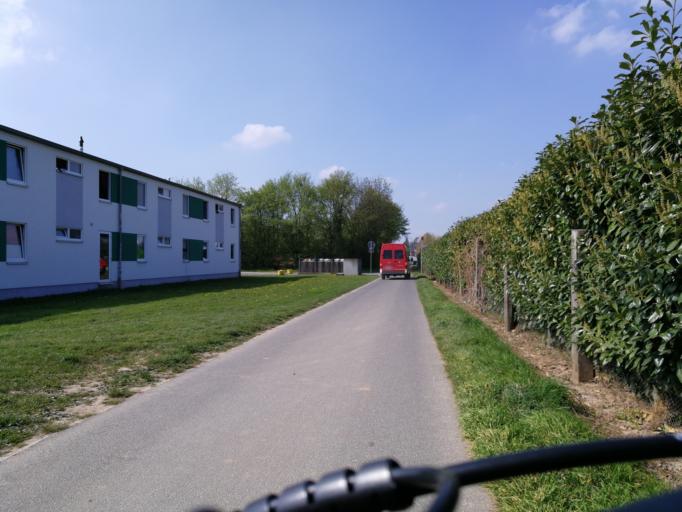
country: DE
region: North Rhine-Westphalia
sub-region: Regierungsbezirk Dusseldorf
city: Dormagen
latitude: 51.1186
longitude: 6.7823
